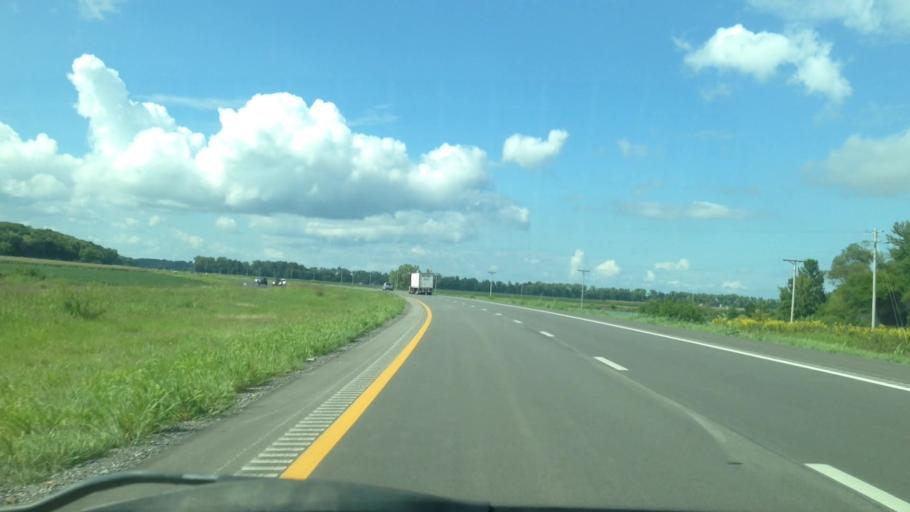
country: US
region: Illinois
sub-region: Adams County
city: Quincy
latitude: 39.9674
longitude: -91.5184
